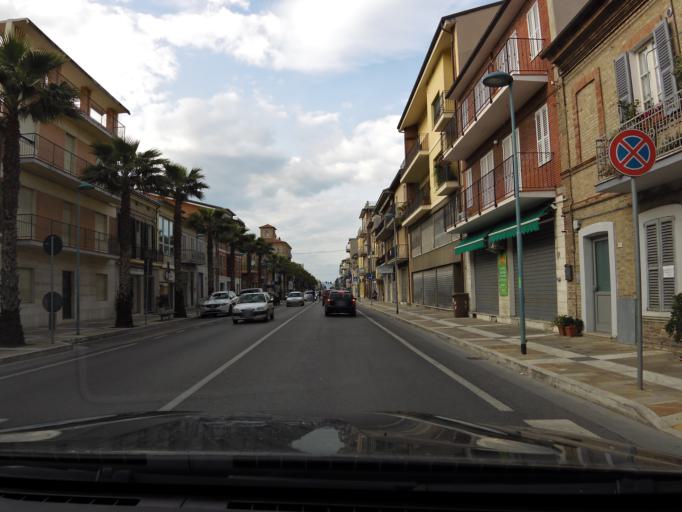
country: IT
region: The Marches
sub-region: Provincia di Macerata
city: Porto Potenza Picena
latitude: 43.3585
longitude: 13.6978
